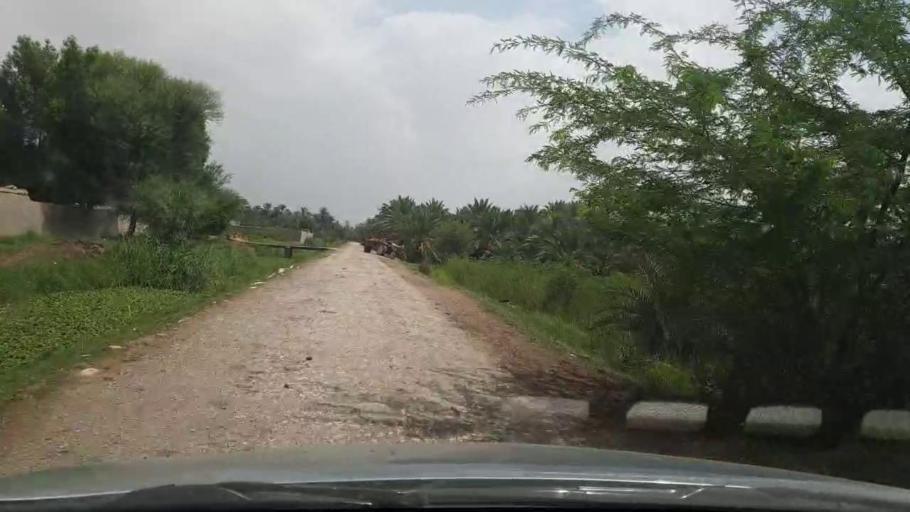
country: PK
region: Sindh
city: Kot Diji
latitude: 27.4123
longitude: 68.7607
